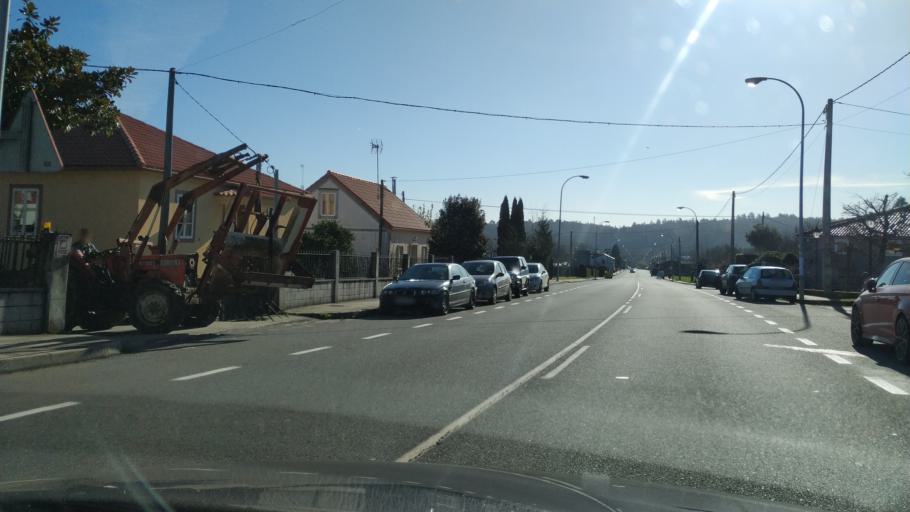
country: ES
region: Galicia
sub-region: Provincia de Pontevedra
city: Silleda
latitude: 42.7392
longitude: -8.3276
